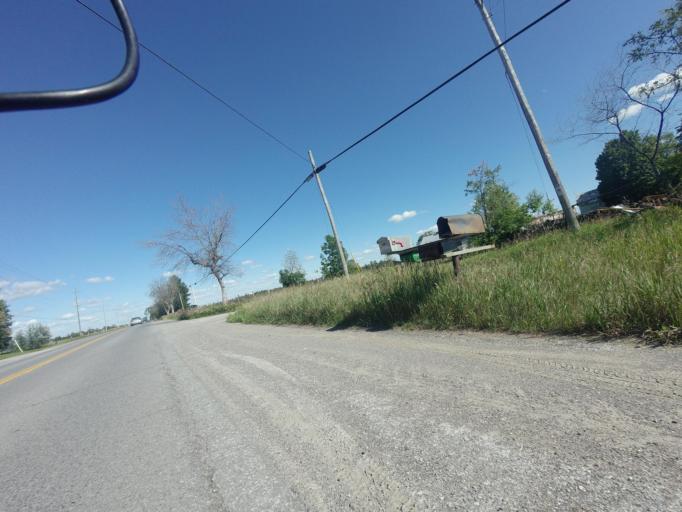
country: CA
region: Ontario
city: Arnprior
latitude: 45.4169
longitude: -76.4217
